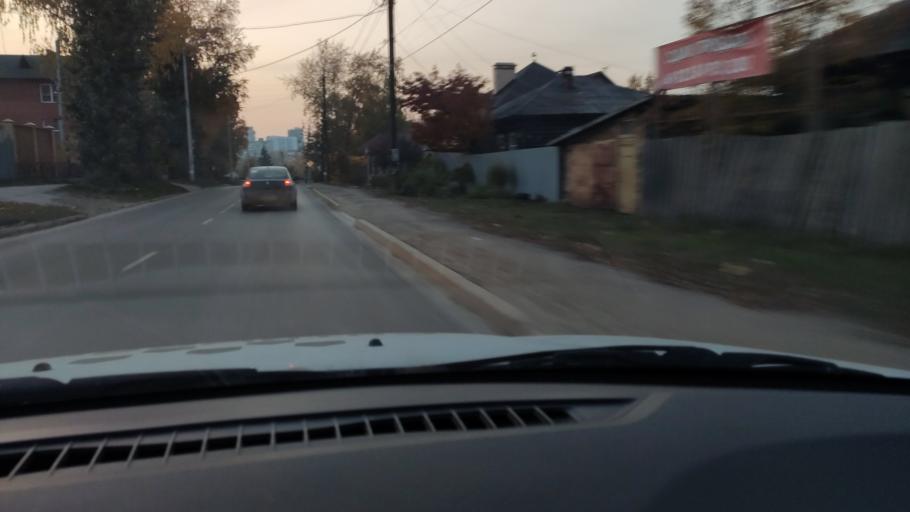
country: RU
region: Perm
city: Perm
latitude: 58.0211
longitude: 56.3148
